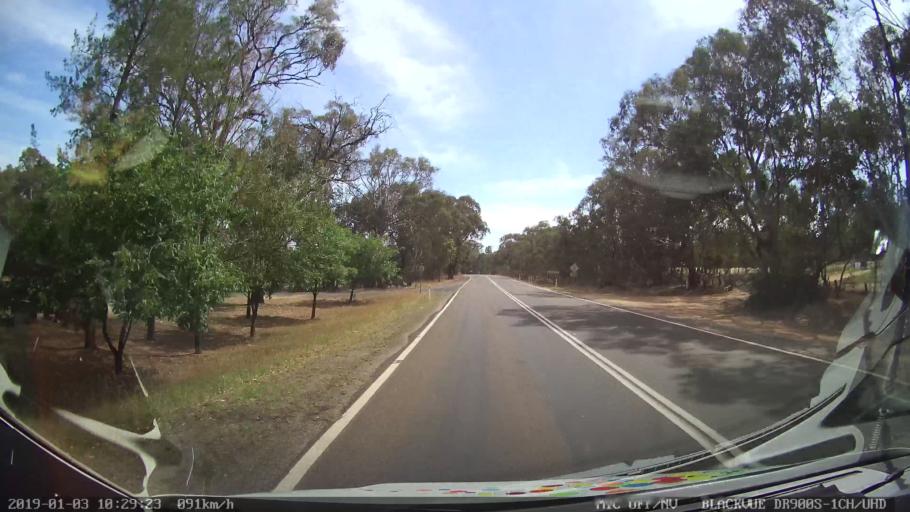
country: AU
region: New South Wales
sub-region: Young
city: Young
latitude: -34.3749
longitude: 148.2601
